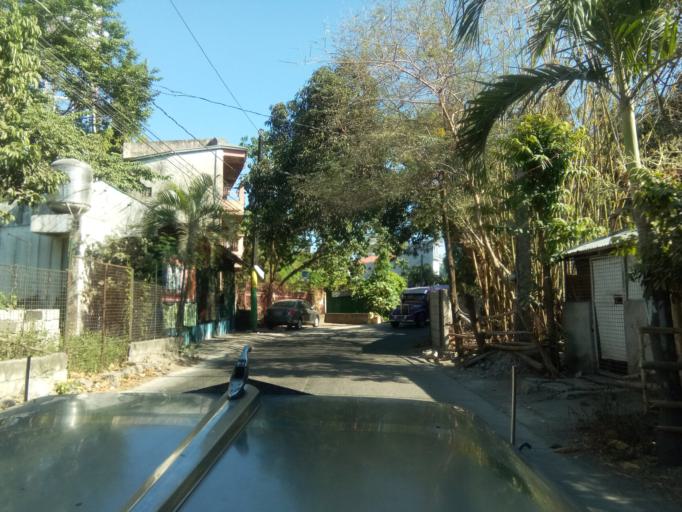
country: PH
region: Calabarzon
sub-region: Province of Cavite
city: Dasmarinas
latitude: 14.3255
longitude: 120.9454
